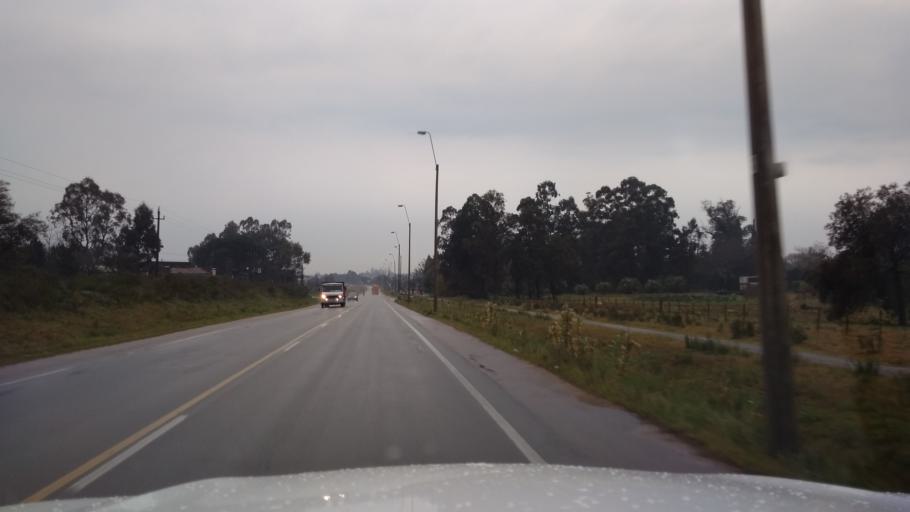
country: UY
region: Canelones
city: Toledo
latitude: -34.7609
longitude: -56.1158
